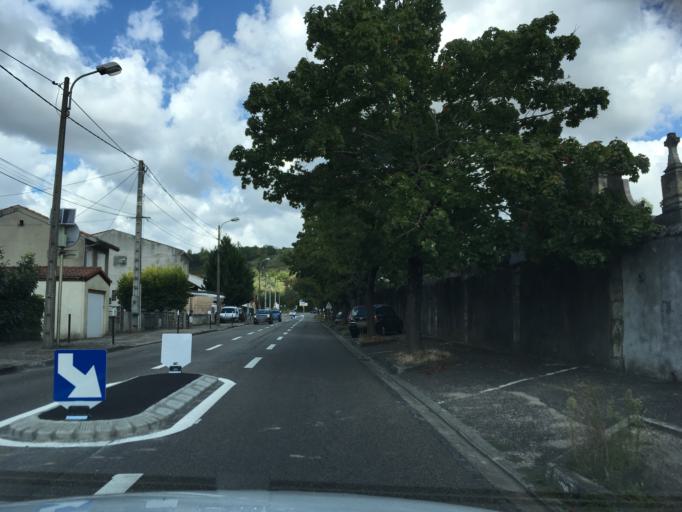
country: FR
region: Aquitaine
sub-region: Departement du Lot-et-Garonne
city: Agen
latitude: 44.2118
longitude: 0.6289
